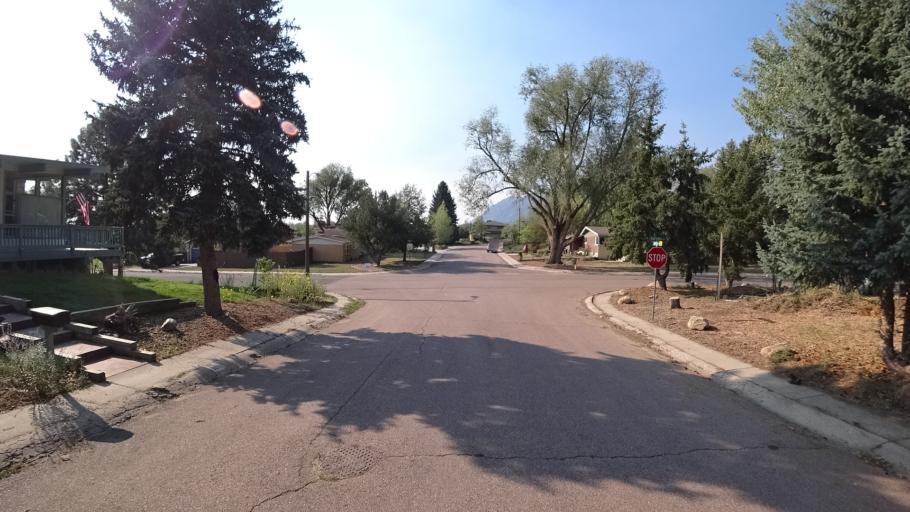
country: US
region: Colorado
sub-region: El Paso County
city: Colorado Springs
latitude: 38.8045
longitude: -104.8461
